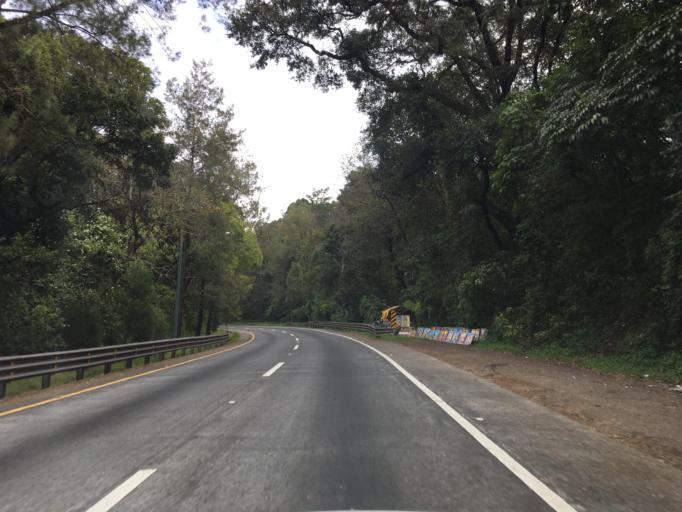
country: GT
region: Sacatepequez
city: Santa Lucia Milpas Altas
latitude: 14.5664
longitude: -90.6786
